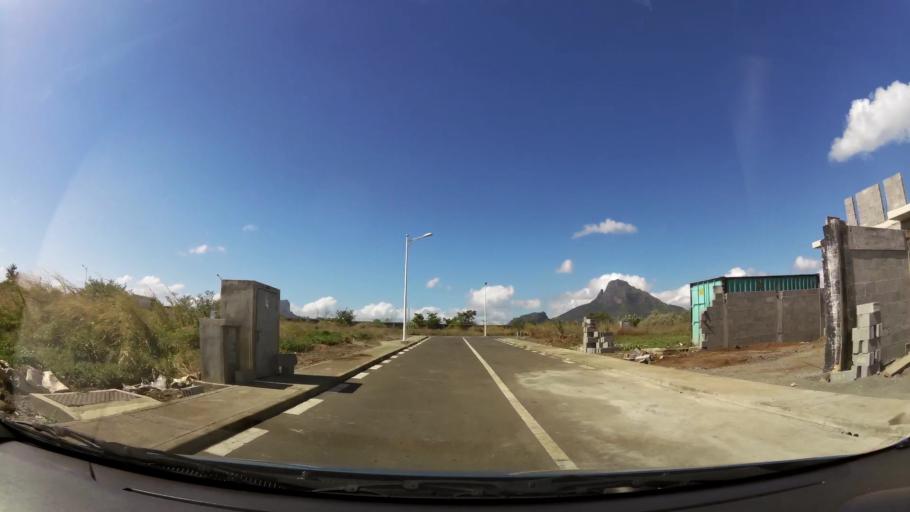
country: MU
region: Black River
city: Flic en Flac
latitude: -20.2785
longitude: 57.3849
